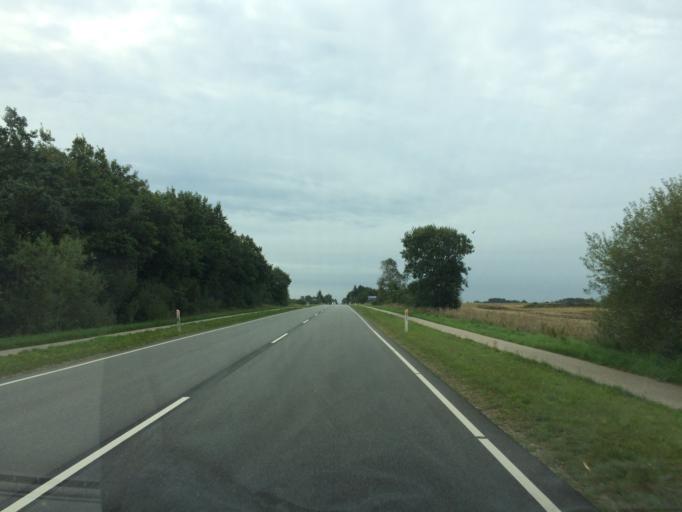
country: DK
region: Central Jutland
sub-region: Herning Kommune
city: Lind
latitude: 56.0776
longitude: 8.9850
